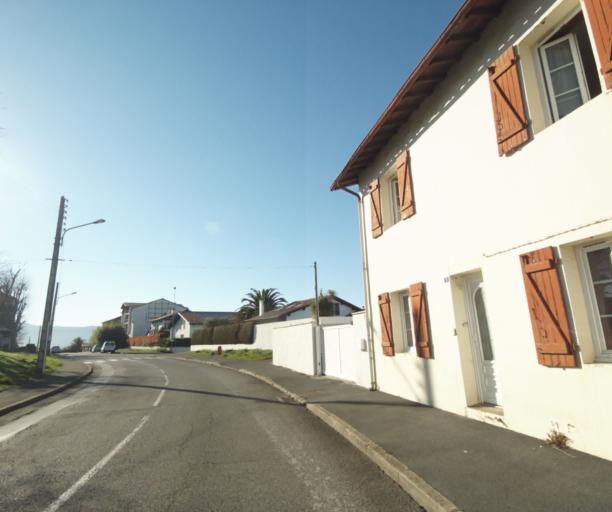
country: FR
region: Aquitaine
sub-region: Departement des Pyrenees-Atlantiques
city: Hendaye
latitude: 43.3629
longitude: -1.7586
